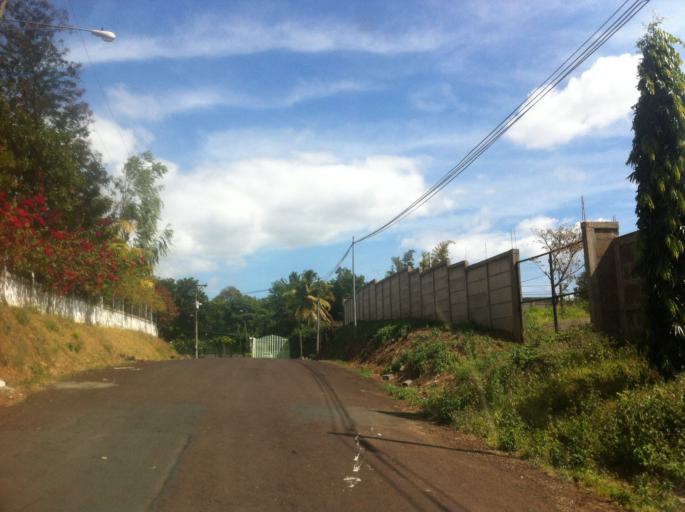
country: NI
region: Managua
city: El Crucero
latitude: 12.0745
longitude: -86.3234
